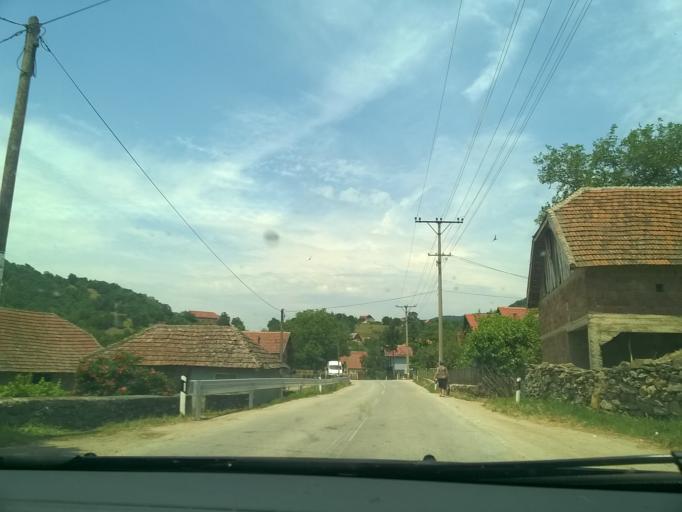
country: RS
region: Central Serbia
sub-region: Nisavski Okrug
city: Aleksinac
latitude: 43.6353
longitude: 21.7177
